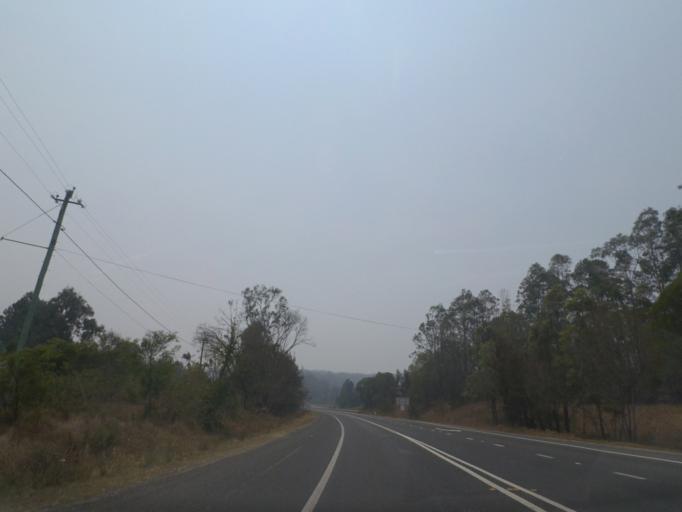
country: AU
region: New South Wales
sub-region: Clarence Valley
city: Maclean
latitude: -29.5645
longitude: 153.1442
